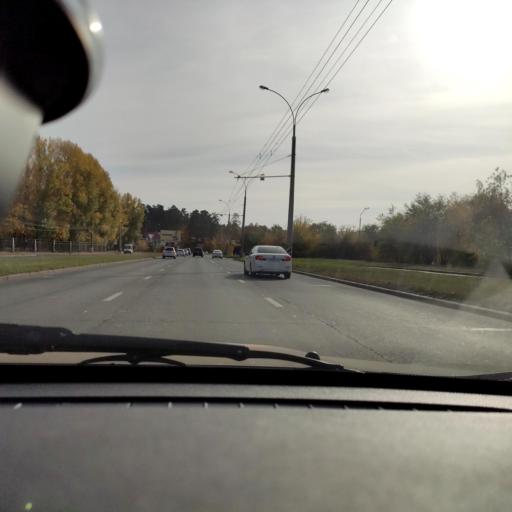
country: RU
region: Samara
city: Tol'yatti
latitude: 53.5009
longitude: 49.2987
